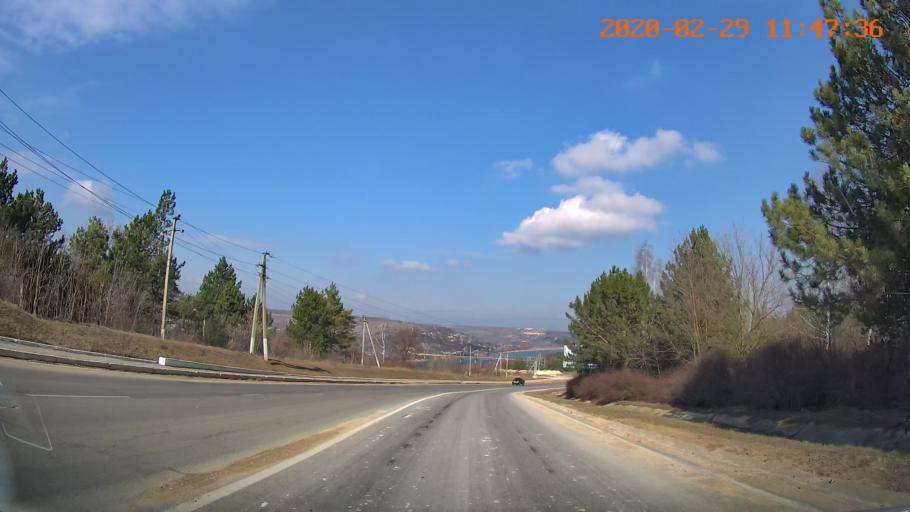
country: MD
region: Rezina
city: Rezina
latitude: 47.7426
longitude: 28.9873
